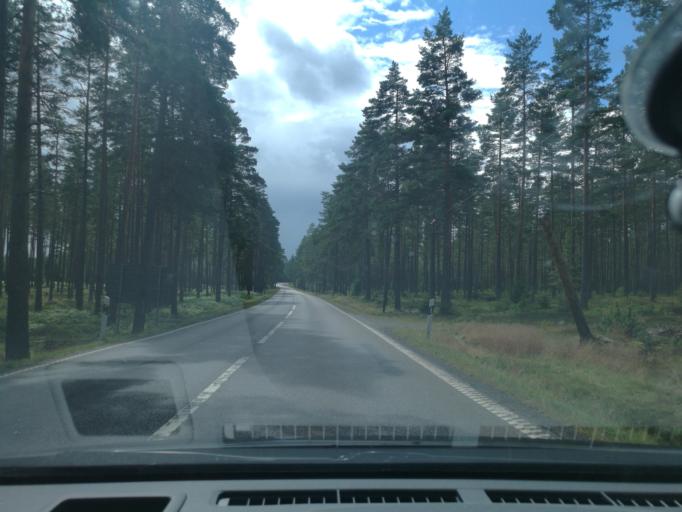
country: SE
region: OErebro
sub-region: Hallsbergs Kommun
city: Palsboda
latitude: 58.8885
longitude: 15.4274
